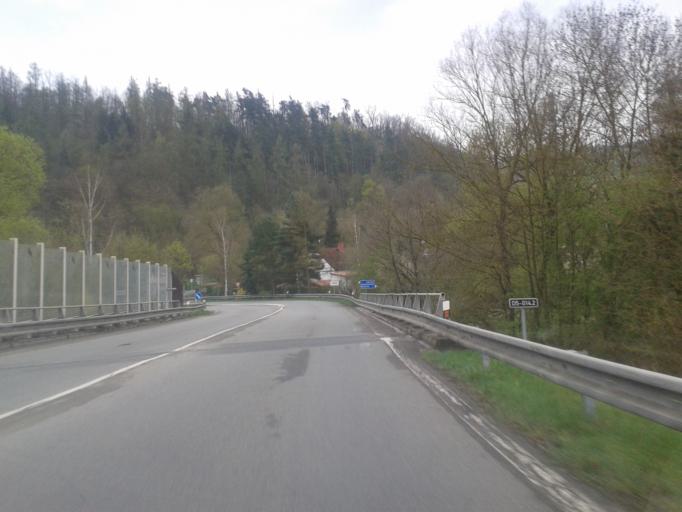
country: CZ
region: Central Bohemia
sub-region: Okres Beroun
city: Lodenice
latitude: 49.9920
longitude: 14.1590
